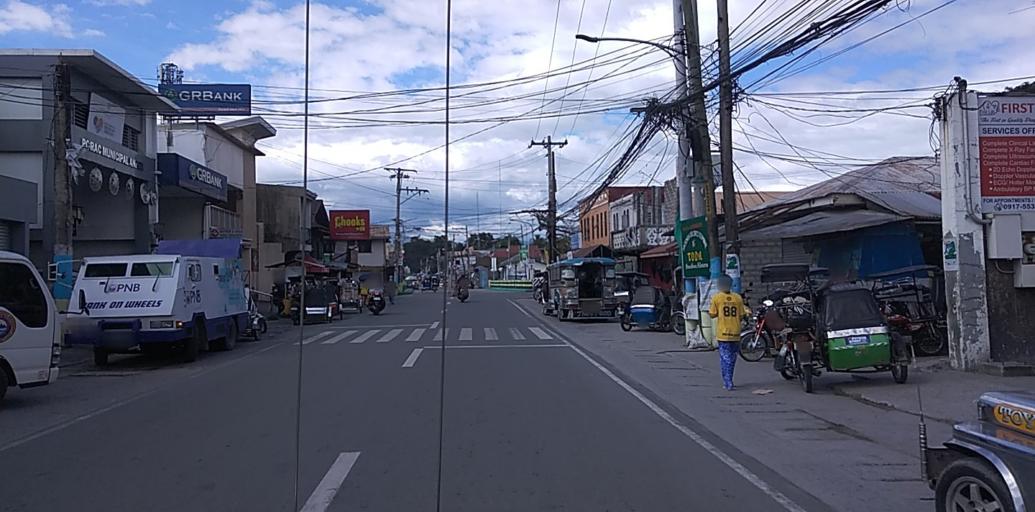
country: PH
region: Central Luzon
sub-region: Province of Pampanga
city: Porac
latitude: 15.0718
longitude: 120.5428
